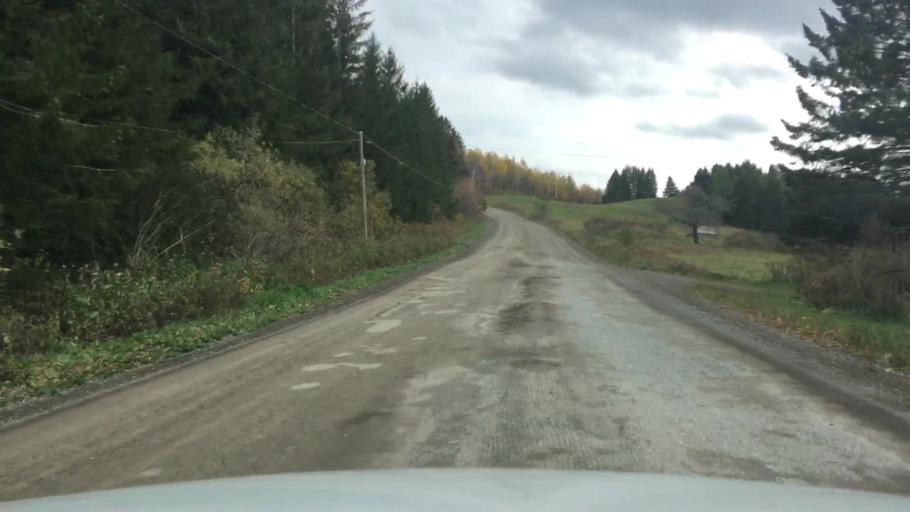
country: US
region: Maine
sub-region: Aroostook County
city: Easton
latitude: 46.5199
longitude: -67.8869
